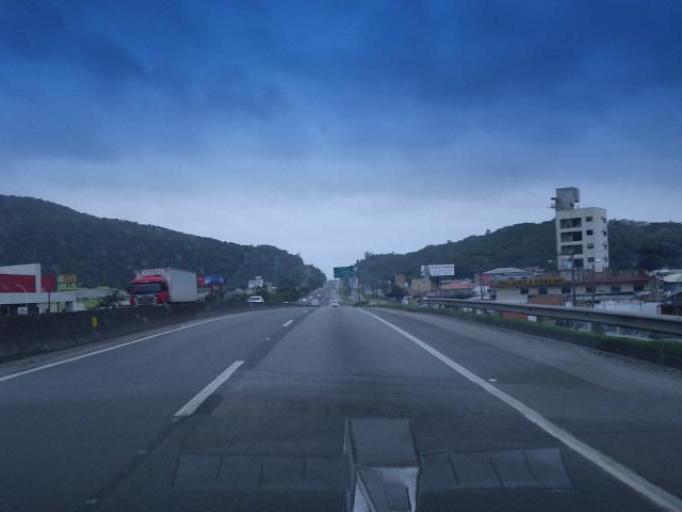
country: BR
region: Santa Catarina
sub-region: Itapema
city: Itapema
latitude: -27.0901
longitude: -48.6150
